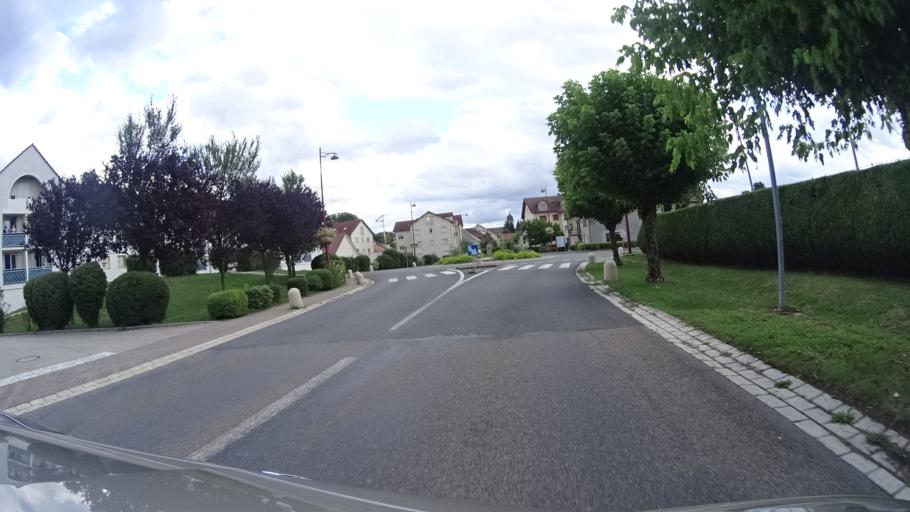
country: FR
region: Franche-Comte
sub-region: Departement du Doubs
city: Saone
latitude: 47.2280
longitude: 6.1140
